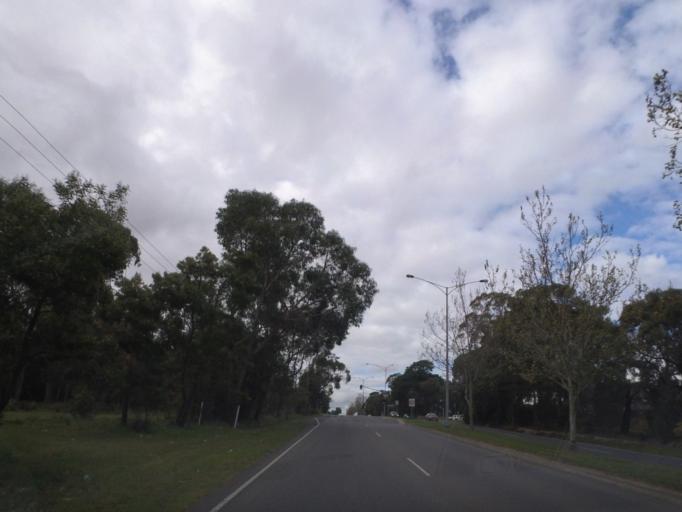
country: AU
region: Victoria
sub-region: Knox
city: Wantirna
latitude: -37.8530
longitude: 145.2208
